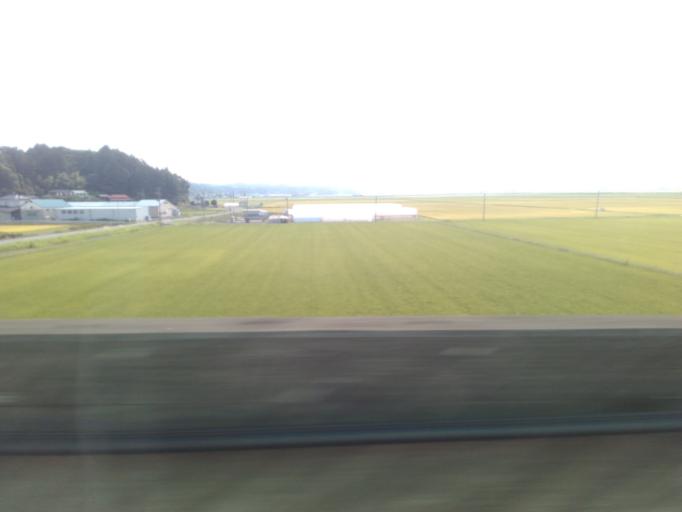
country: JP
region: Iwate
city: Ichinoseki
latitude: 38.8024
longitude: 141.0969
